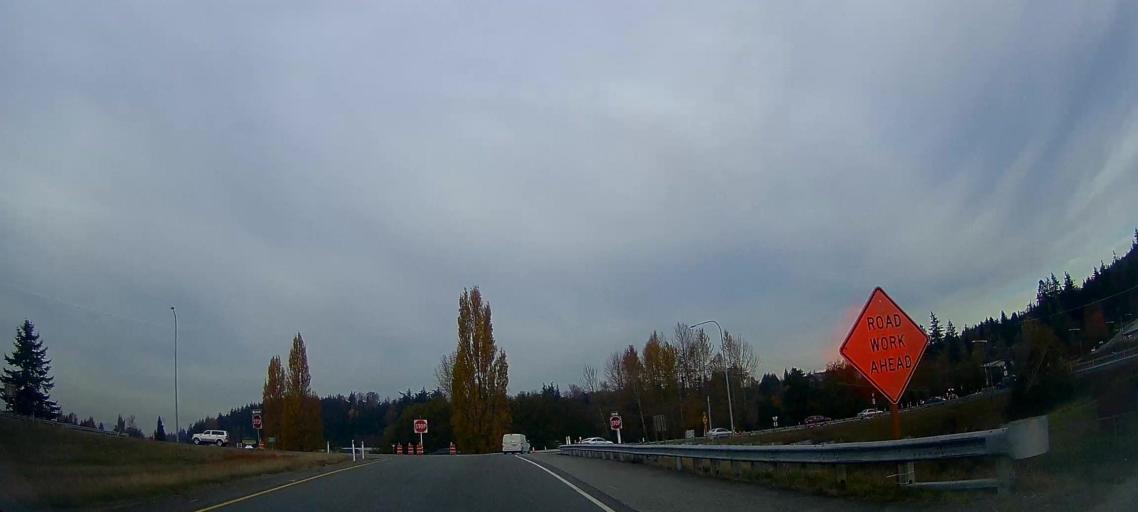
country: US
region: Washington
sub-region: Skagit County
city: Mount Vernon
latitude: 48.3987
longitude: -122.3294
